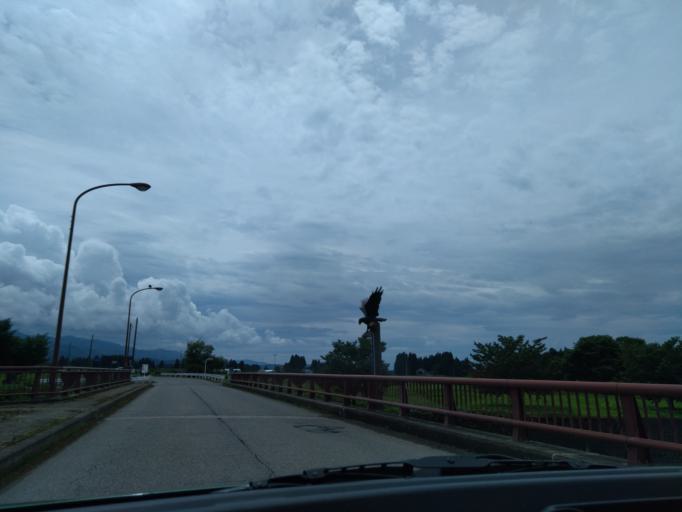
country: JP
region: Akita
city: Kakunodatemachi
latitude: 39.5341
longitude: 140.6410
